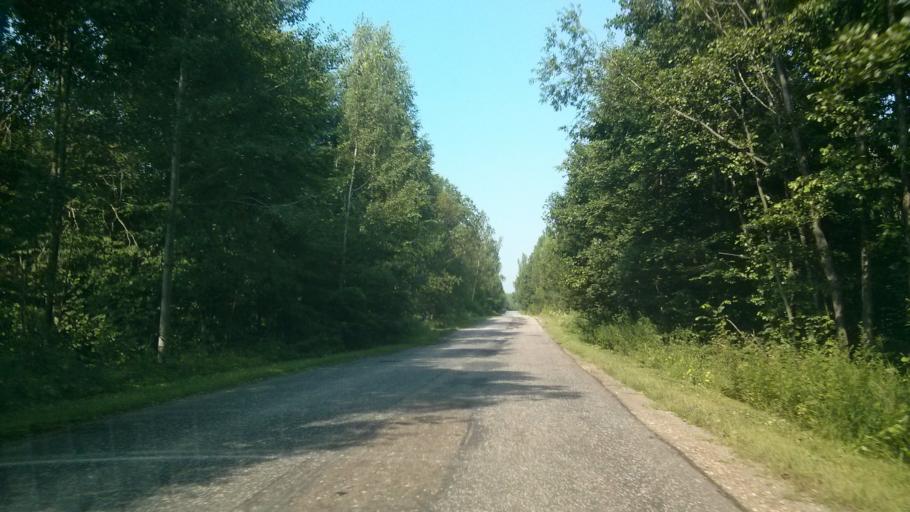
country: RU
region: Vladimir
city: Murom
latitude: 55.5053
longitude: 42.0100
